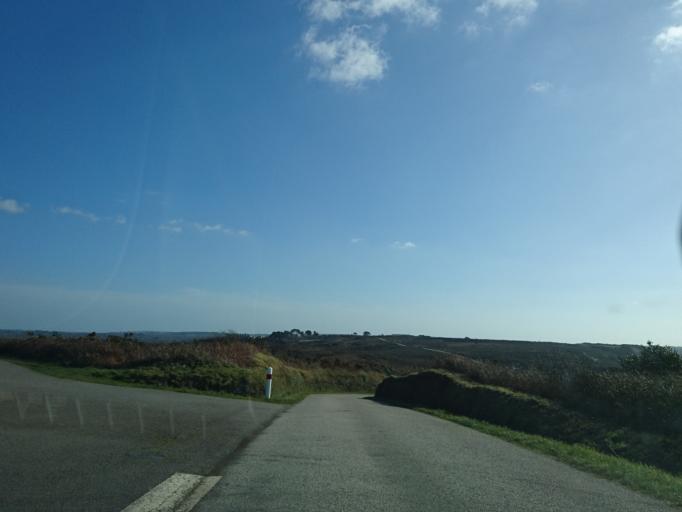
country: FR
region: Brittany
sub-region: Departement du Finistere
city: Roscanvel
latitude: 48.3122
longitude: -4.5706
